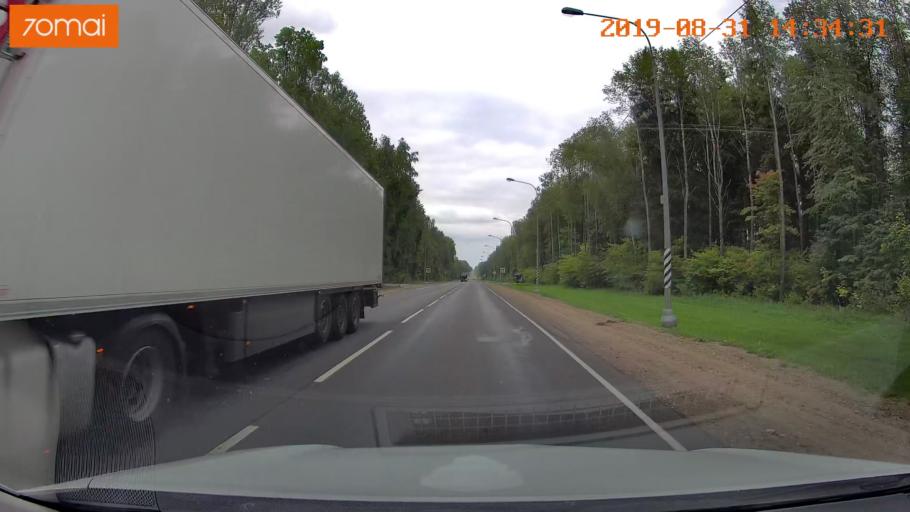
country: RU
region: Smolensk
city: Yekimovichi
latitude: 54.1578
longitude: 33.4389
